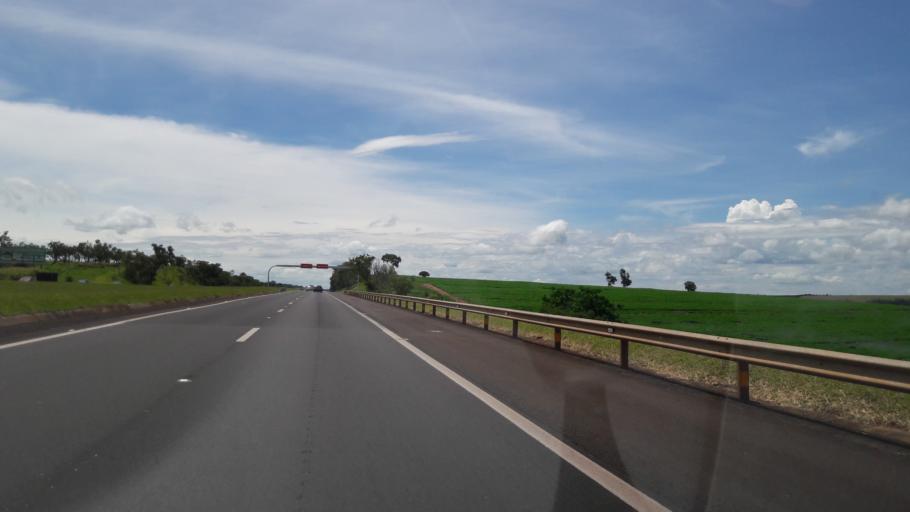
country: BR
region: Sao Paulo
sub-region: Avare
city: Avare
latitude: -22.9770
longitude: -48.7835
